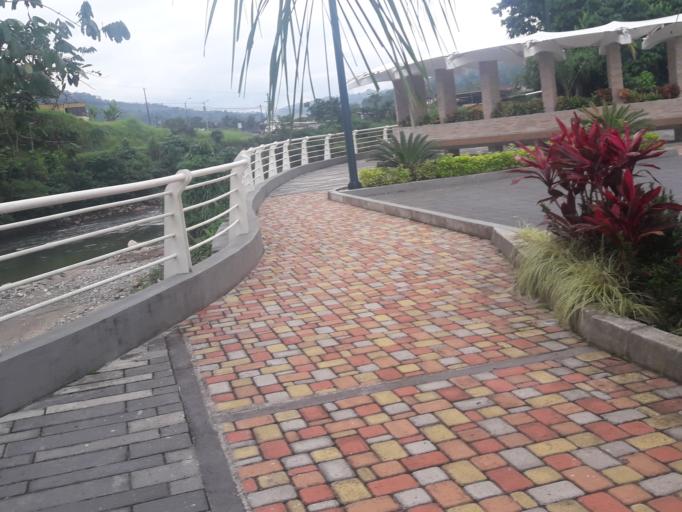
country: EC
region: Napo
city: Tena
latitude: -0.9898
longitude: -77.8133
